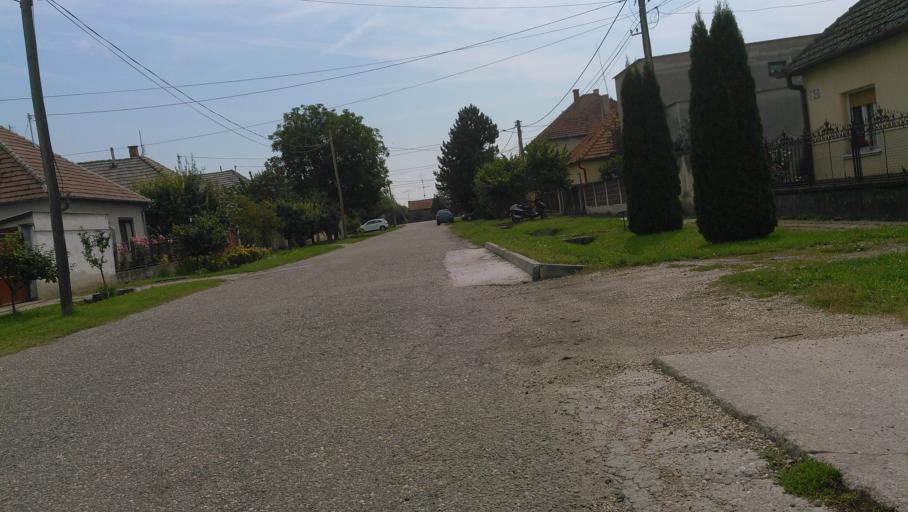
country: SK
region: Nitriansky
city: Kolarovo
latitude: 47.9087
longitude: 17.9938
